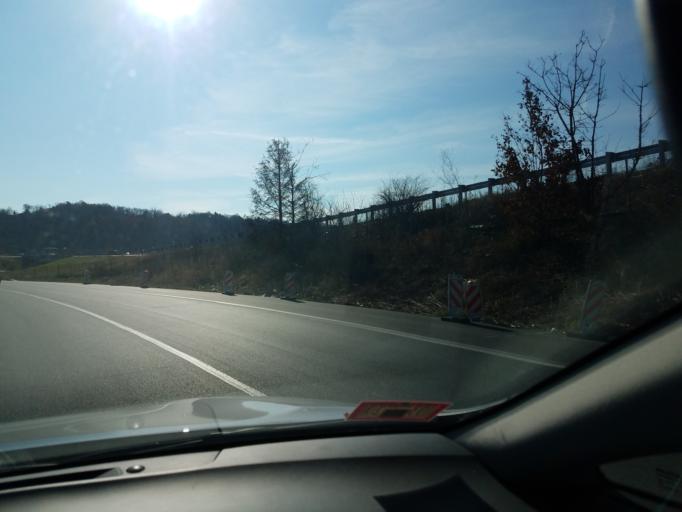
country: US
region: Pennsylvania
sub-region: Allegheny County
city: Ben Avon
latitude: 40.5277
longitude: -80.0713
